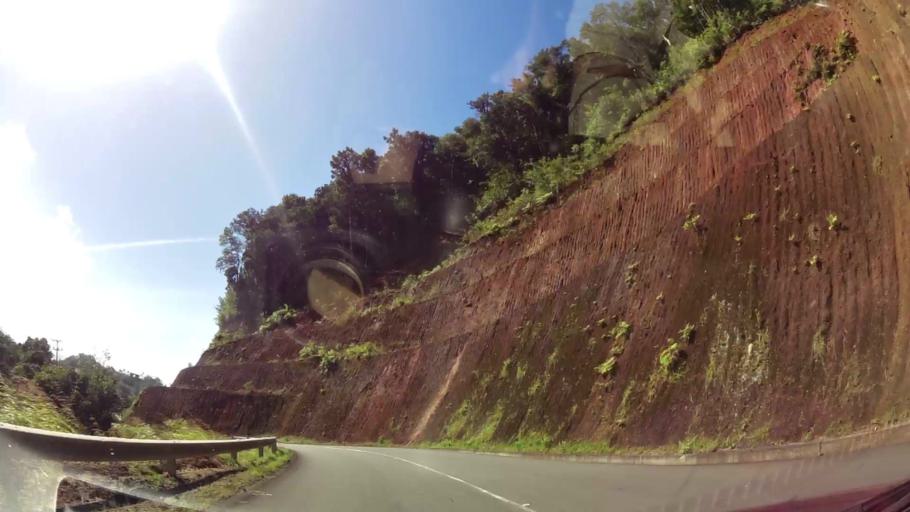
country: DM
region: Saint Paul
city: Pont Casse
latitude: 15.3507
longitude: -61.3617
